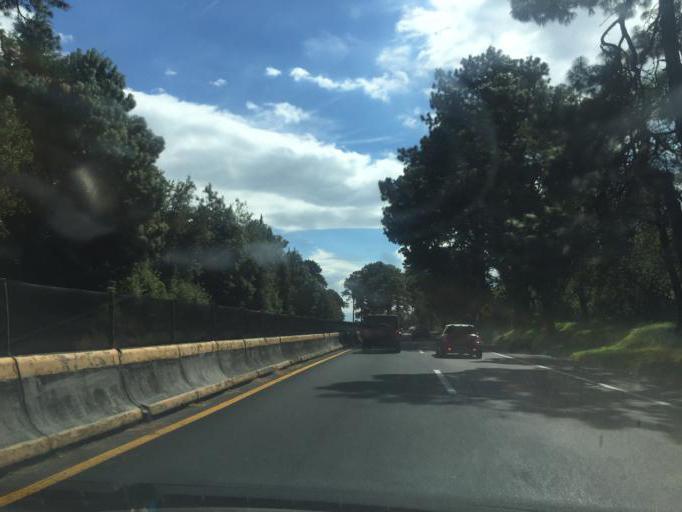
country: MX
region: Morelos
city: Tres Marias
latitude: 19.0314
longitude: -99.2154
